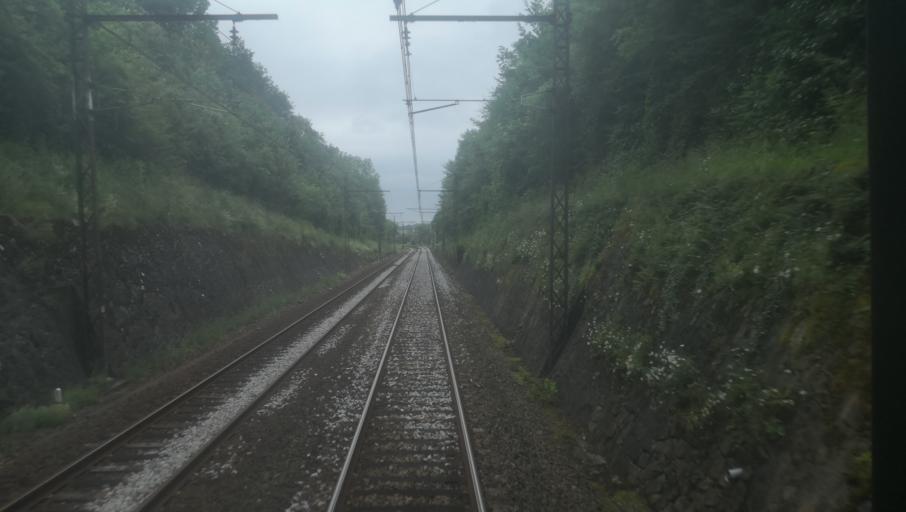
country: FR
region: Centre
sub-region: Departement de l'Indre
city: Le Pechereau
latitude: 46.5270
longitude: 1.5231
